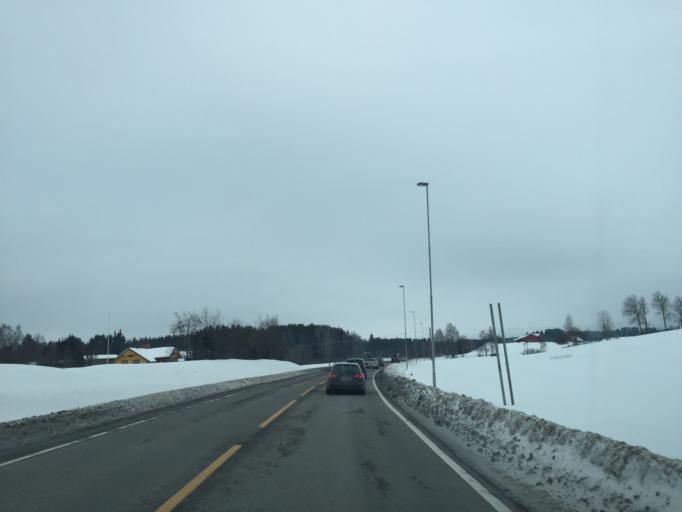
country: NO
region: Hedmark
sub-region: Loten
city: Loten
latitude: 60.8029
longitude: 11.2923
